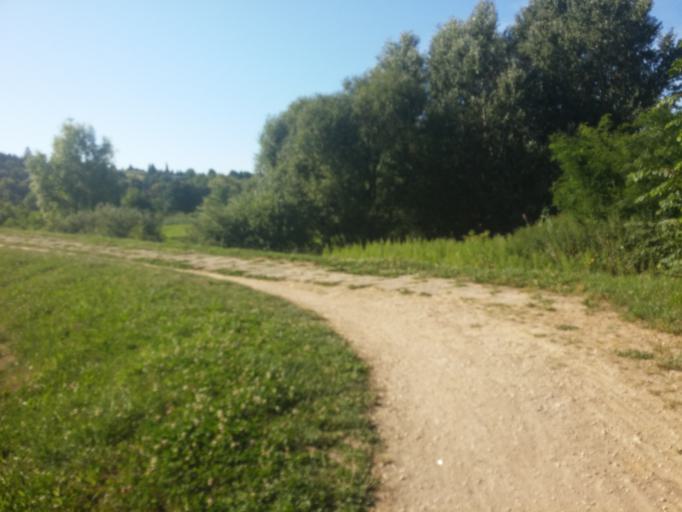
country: HU
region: Zala
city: Nagykanizsa
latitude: 46.4458
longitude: 17.0326
